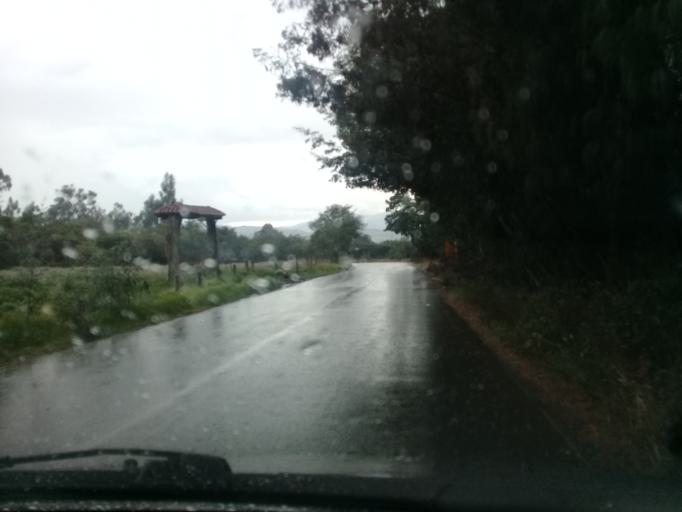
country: CO
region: Cundinamarca
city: Guasca
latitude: 4.8528
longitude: -73.8483
